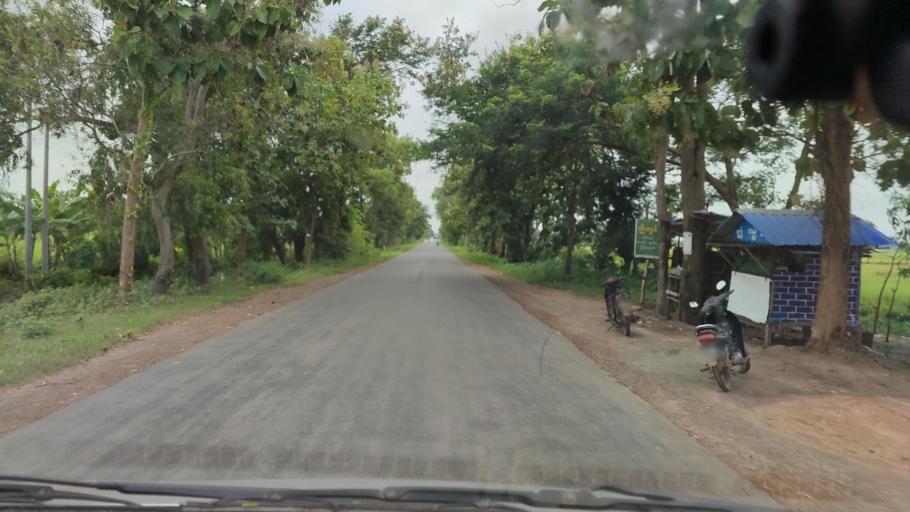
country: MM
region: Bago
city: Pyay
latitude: 18.8604
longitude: 95.4056
